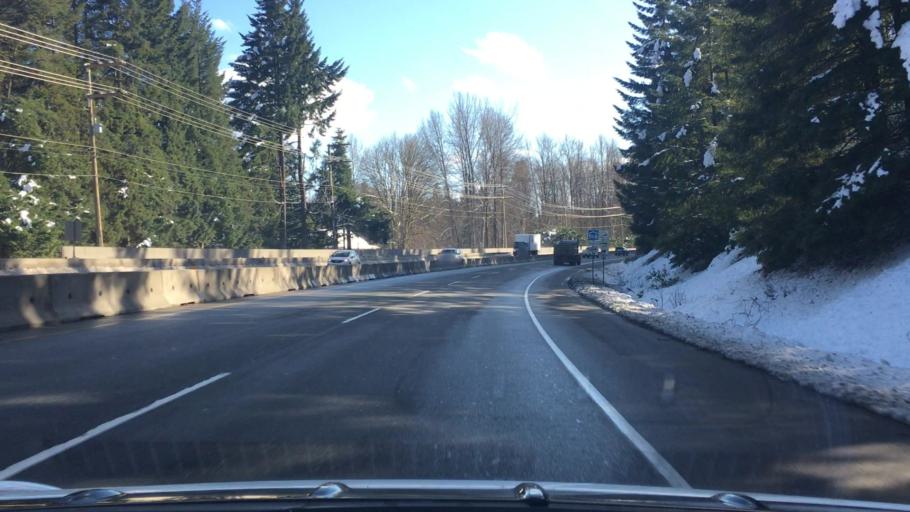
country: CA
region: British Columbia
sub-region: Cowichan Valley Regional District
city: Ladysmith
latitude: 49.0663
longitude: -123.8776
